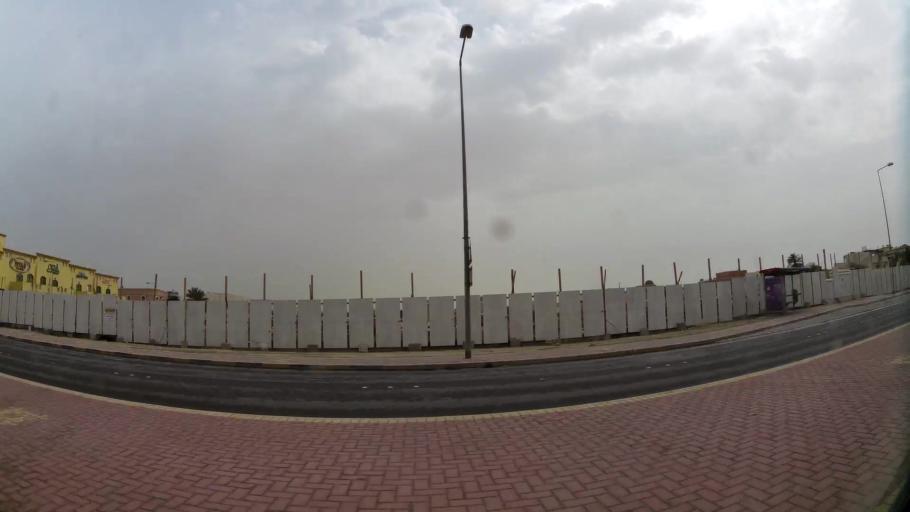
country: BH
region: Northern
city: Ar Rifa'
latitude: 26.1347
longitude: 50.5488
